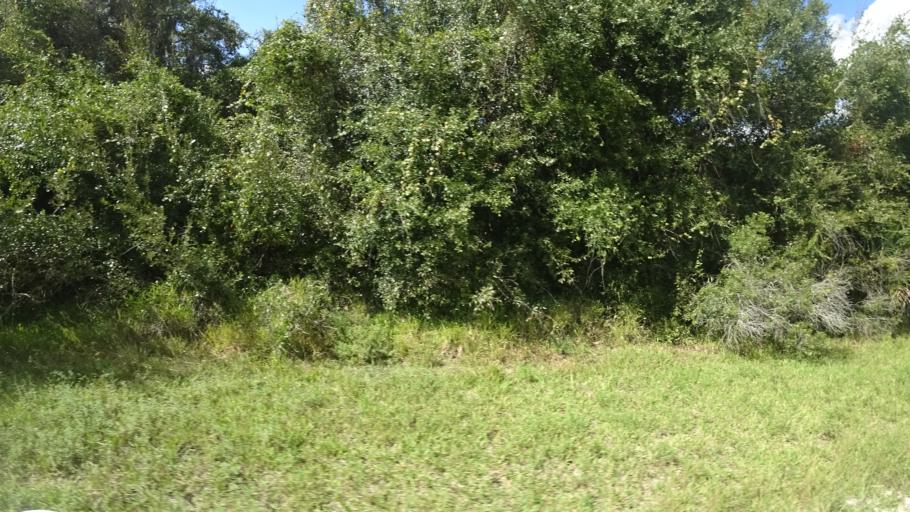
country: US
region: Florida
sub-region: Sarasota County
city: Warm Mineral Springs
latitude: 27.2694
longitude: -82.1545
